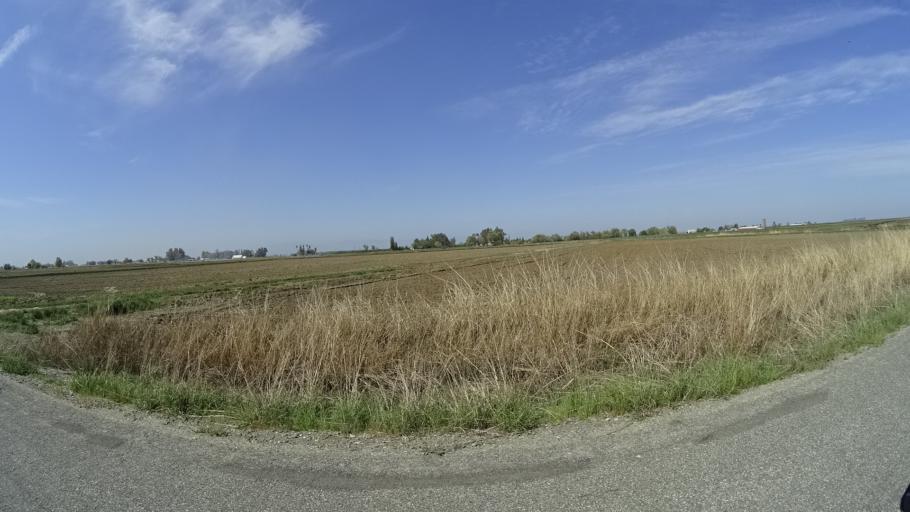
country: US
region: California
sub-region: Glenn County
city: Hamilton City
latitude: 39.6005
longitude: -122.0461
